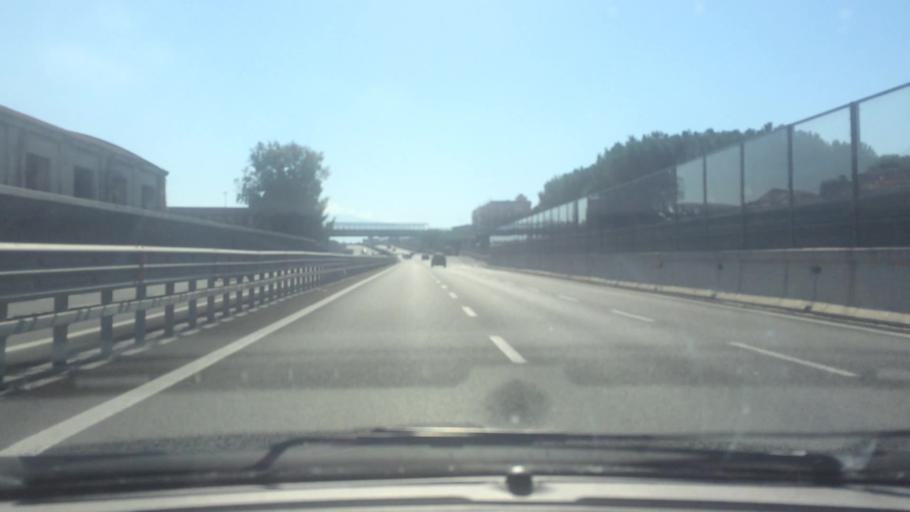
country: IT
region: Campania
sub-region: Provincia di Napoli
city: Ercolano
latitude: 40.8190
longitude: 14.3531
